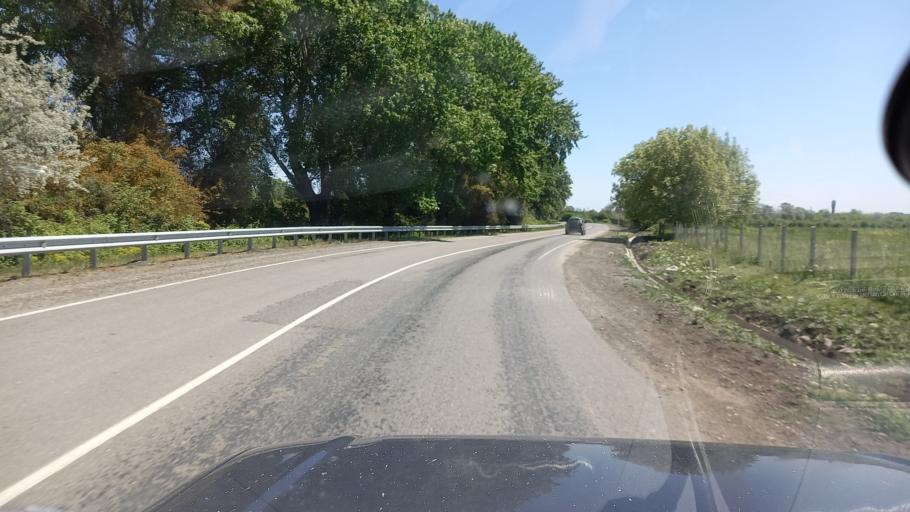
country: RU
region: Dagestan
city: Samur
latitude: 41.7339
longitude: 48.4657
